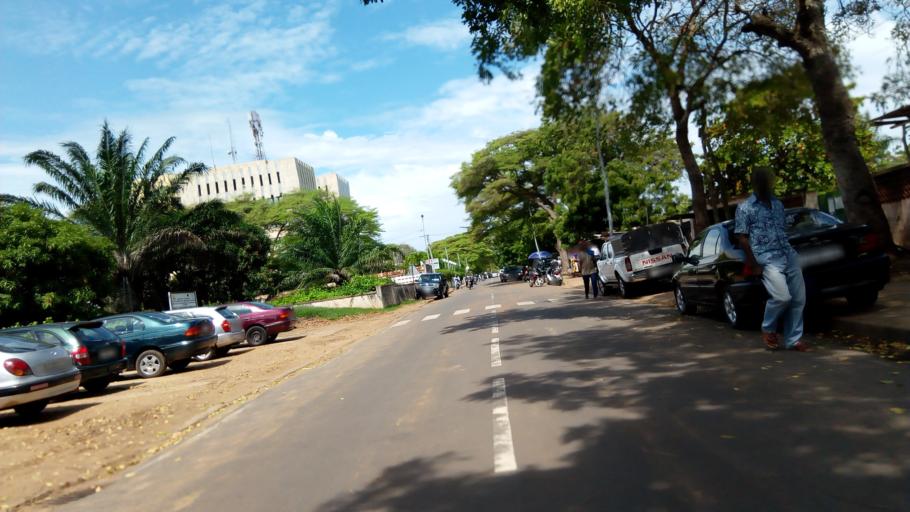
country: TG
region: Maritime
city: Lome
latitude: 6.1252
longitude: 1.2105
